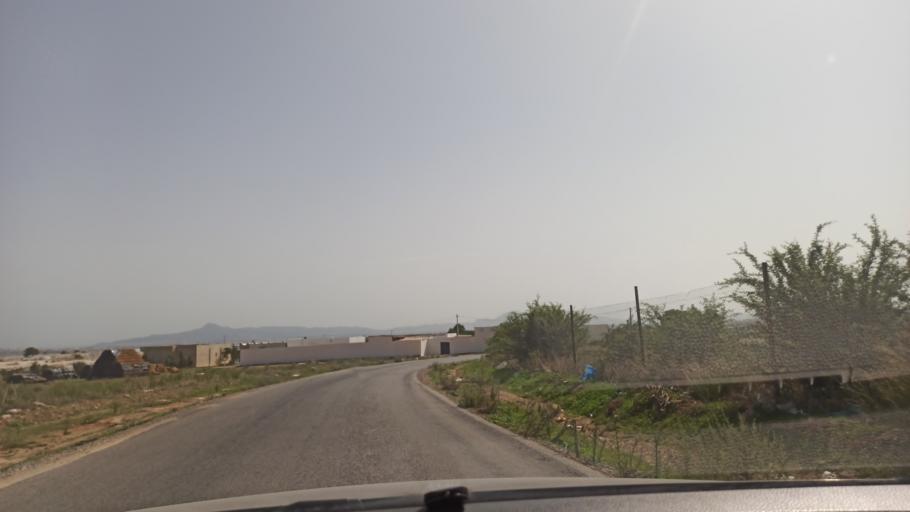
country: TN
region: Manouba
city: Manouba
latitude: 36.7339
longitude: 10.0931
